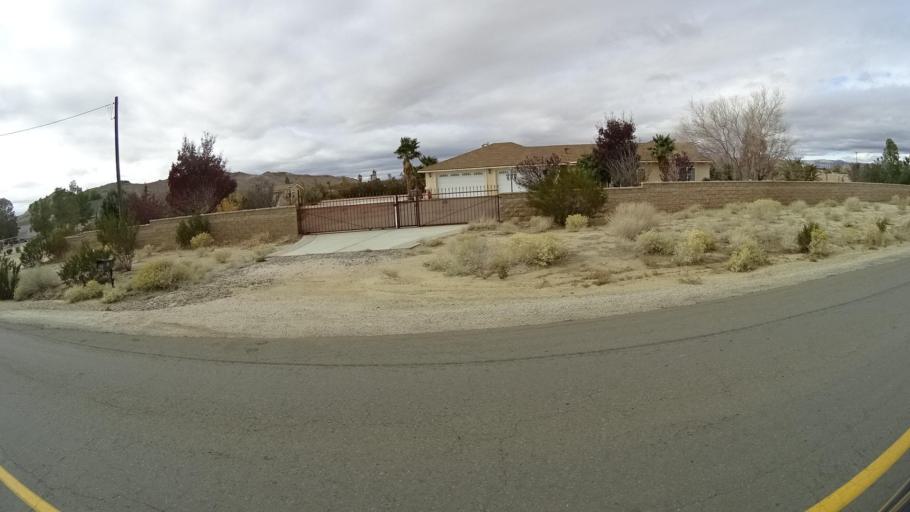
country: US
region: California
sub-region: Kern County
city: Rosamond
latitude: 34.9348
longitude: -118.2124
